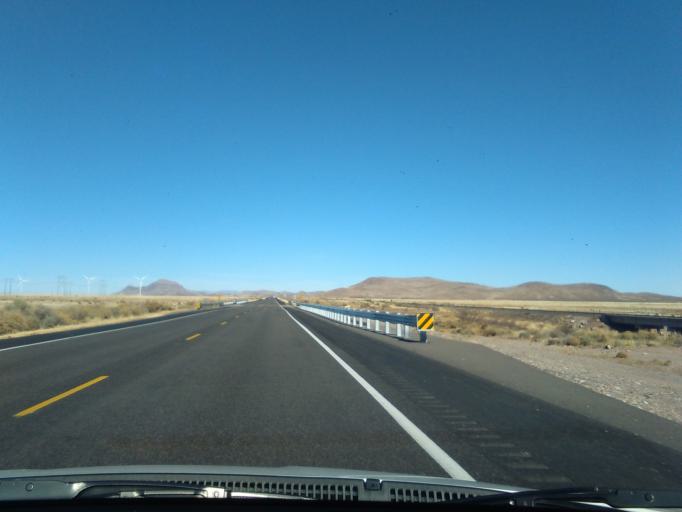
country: US
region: New Mexico
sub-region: Luna County
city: Deming
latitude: 32.5063
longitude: -107.5082
